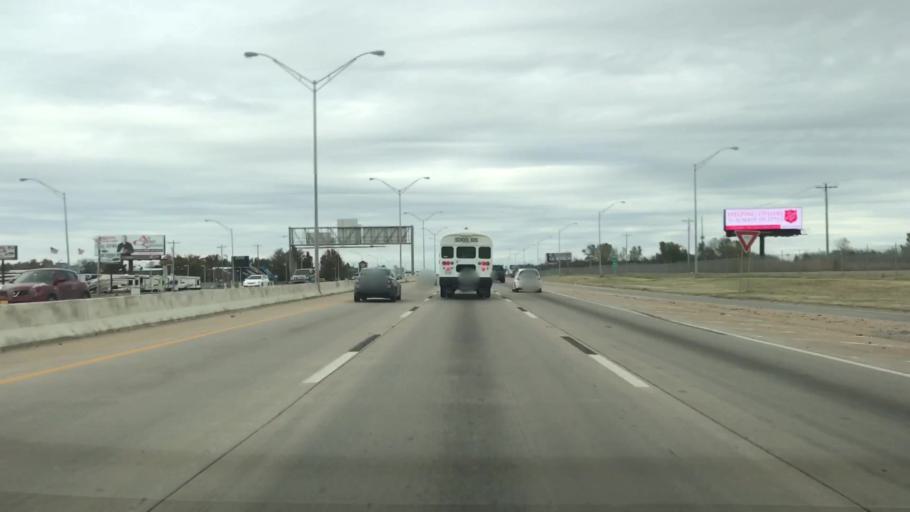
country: US
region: Oklahoma
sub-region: Cleveland County
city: Moore
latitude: 35.3663
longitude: -97.4948
